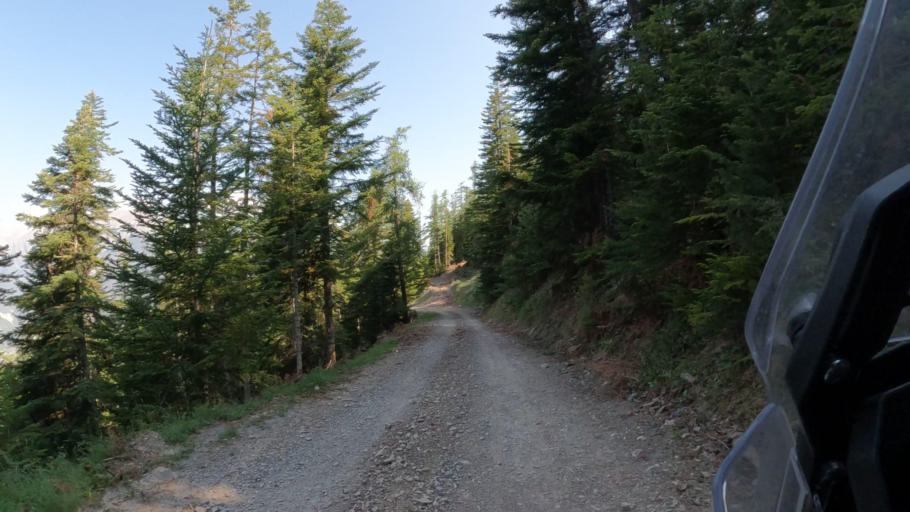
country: FR
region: Provence-Alpes-Cote d'Azur
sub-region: Departement des Hautes-Alpes
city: Embrun
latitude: 44.5896
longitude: 6.5654
